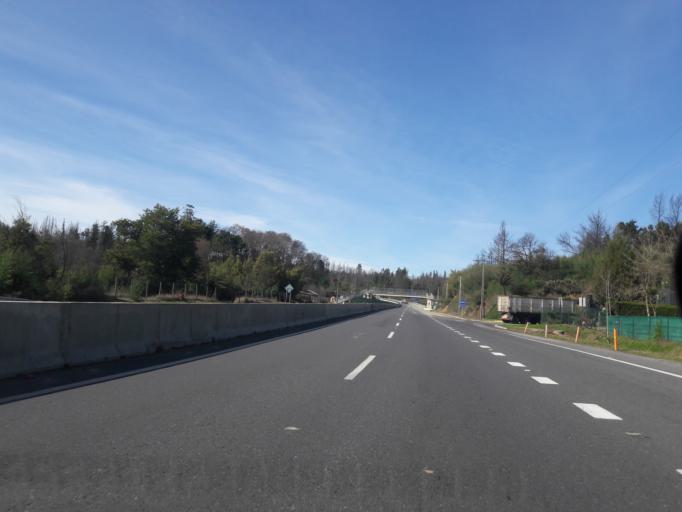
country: CL
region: Biobio
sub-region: Provincia de Concepcion
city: Chiguayante
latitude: -36.8634
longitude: -72.8565
